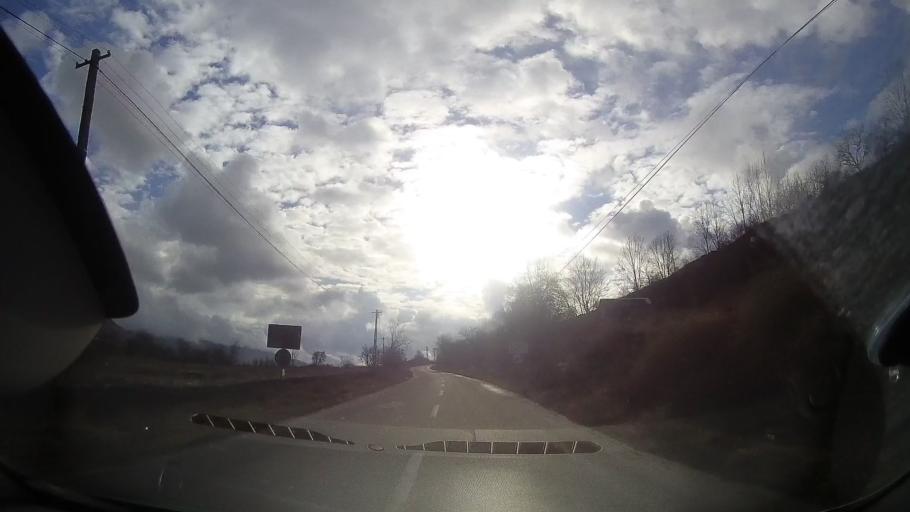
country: RO
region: Alba
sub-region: Comuna Rimetea
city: Rimetea
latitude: 46.4478
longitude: 23.5656
